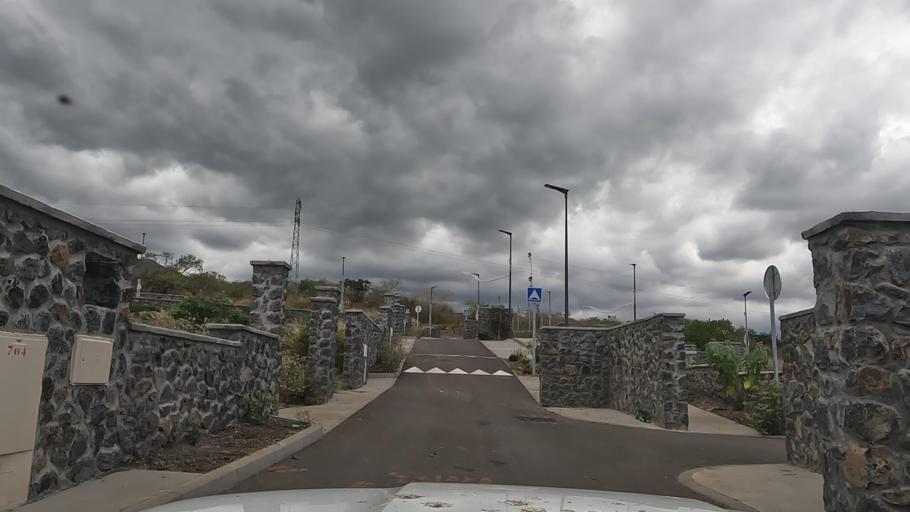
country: RE
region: Reunion
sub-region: Reunion
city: Saint-Louis
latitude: -21.2670
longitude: 55.4154
